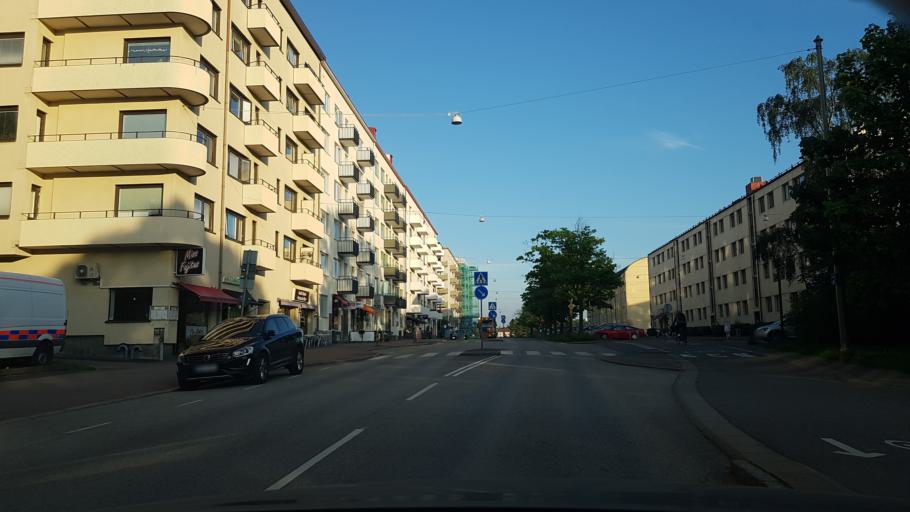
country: SE
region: Vaestra Goetaland
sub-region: Goteborg
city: Goeteborg
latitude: 57.6879
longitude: 11.9821
